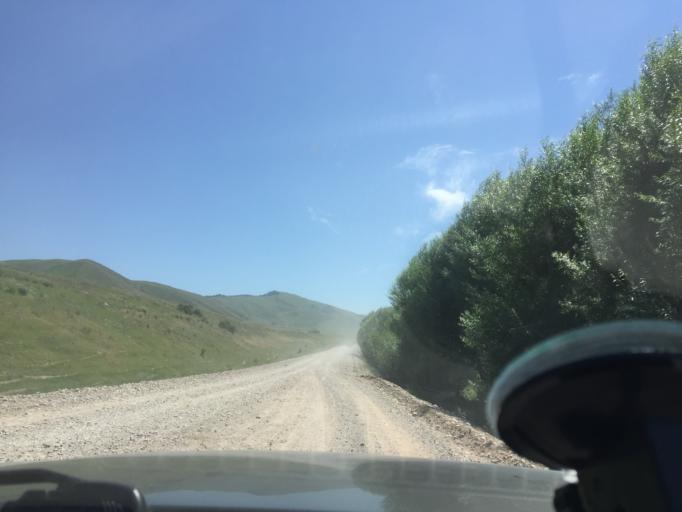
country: KG
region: Ysyk-Koel
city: Teploklyuchenka
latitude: 42.7276
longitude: 78.7864
